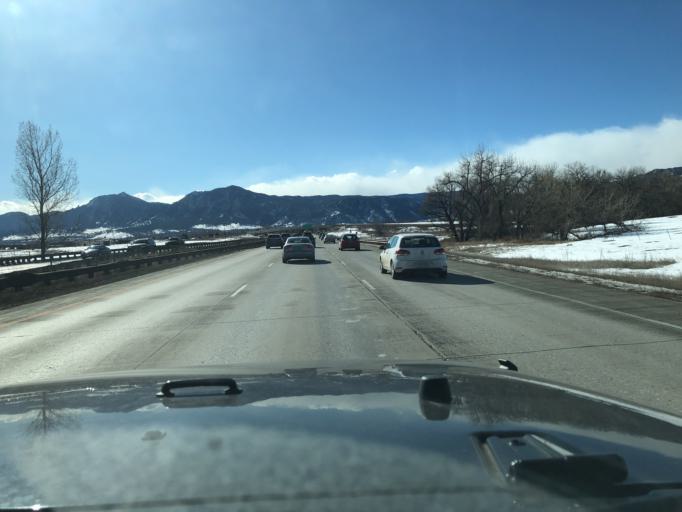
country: US
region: Colorado
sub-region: Boulder County
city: Boulder
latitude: 40.0465
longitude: -105.2393
